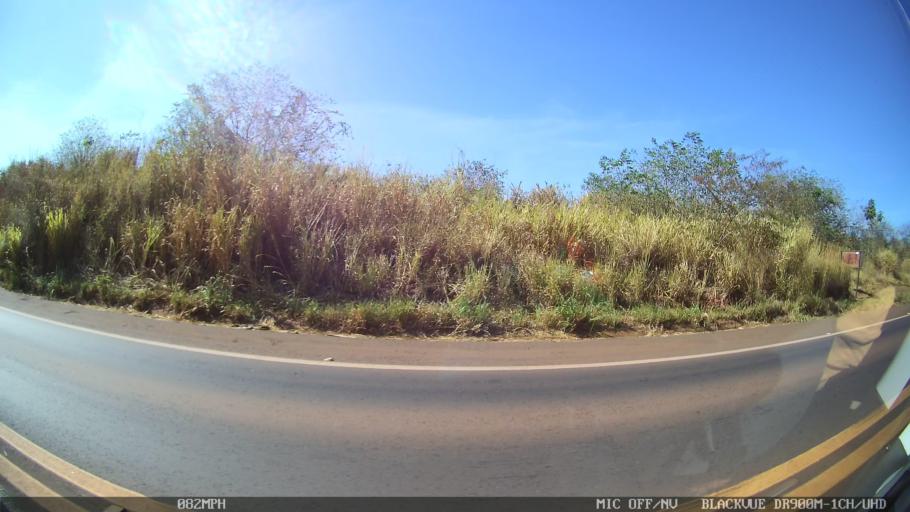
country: BR
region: Sao Paulo
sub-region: Olimpia
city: Olimpia
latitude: -20.7202
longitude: -48.8704
